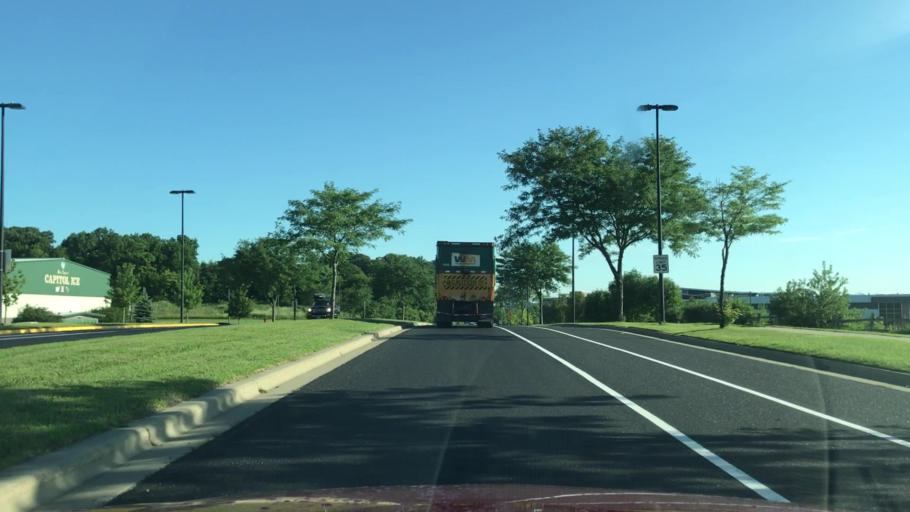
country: US
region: Wisconsin
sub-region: Dane County
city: Middleton
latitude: 43.1037
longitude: -89.5362
